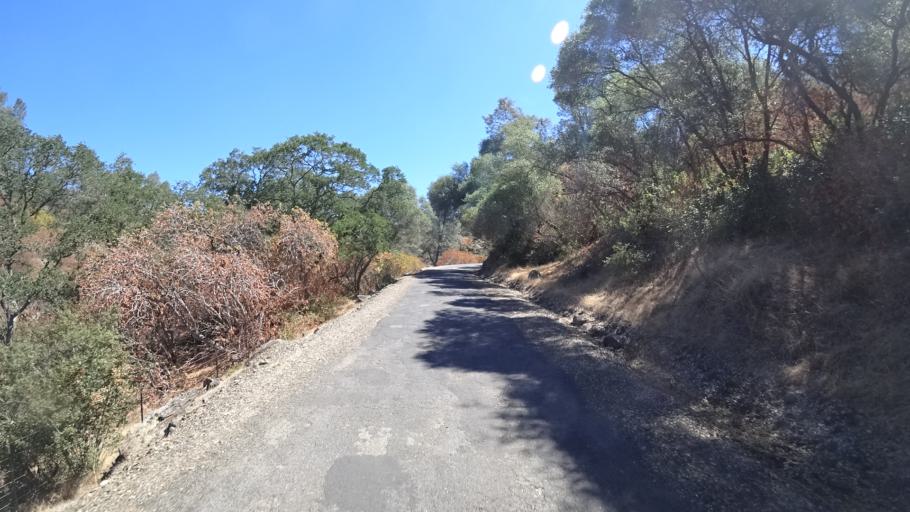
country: US
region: California
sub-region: Calaveras County
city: Rancho Calaveras
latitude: 38.0230
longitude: -120.7733
